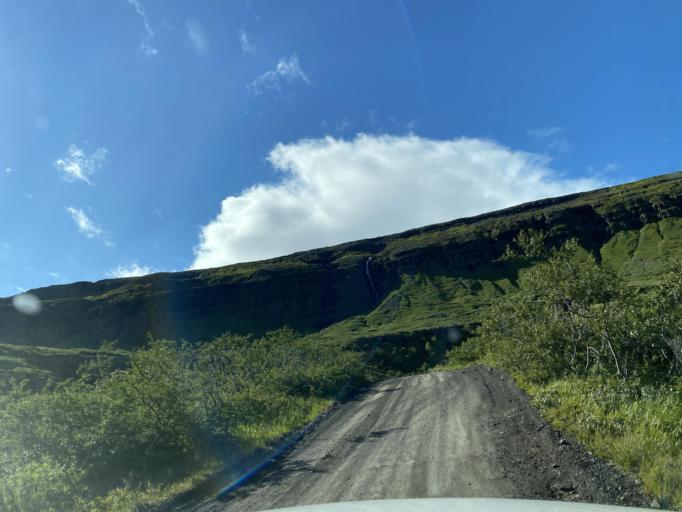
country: IS
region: East
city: Eskifjoerdur
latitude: 65.1821
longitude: -14.0736
